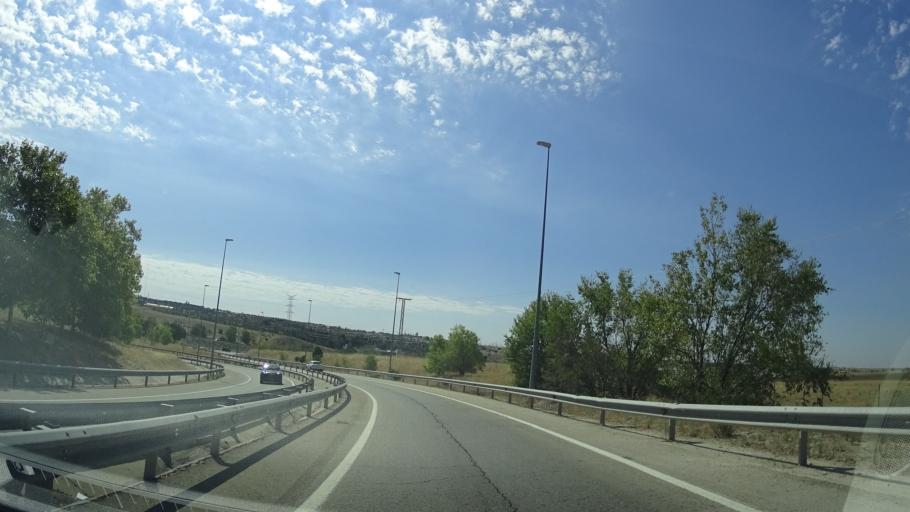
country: ES
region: Madrid
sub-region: Provincia de Madrid
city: Las Rozas de Madrid
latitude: 40.4980
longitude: -3.8969
